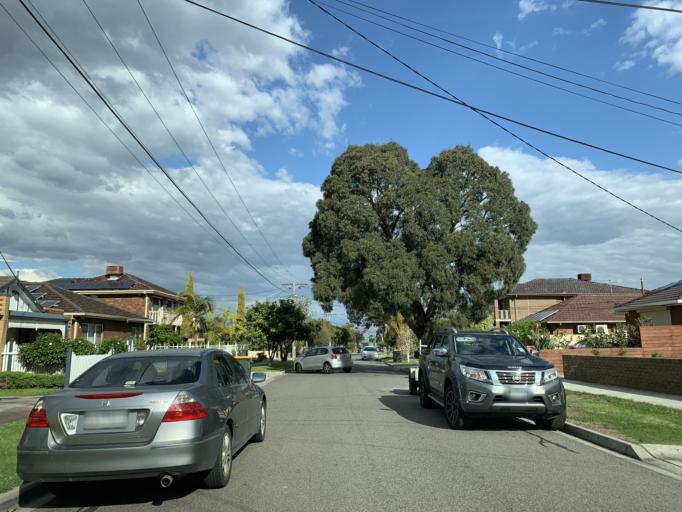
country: AU
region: Victoria
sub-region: Moonee Valley
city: Keilor East
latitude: -37.7471
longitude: 144.8601
